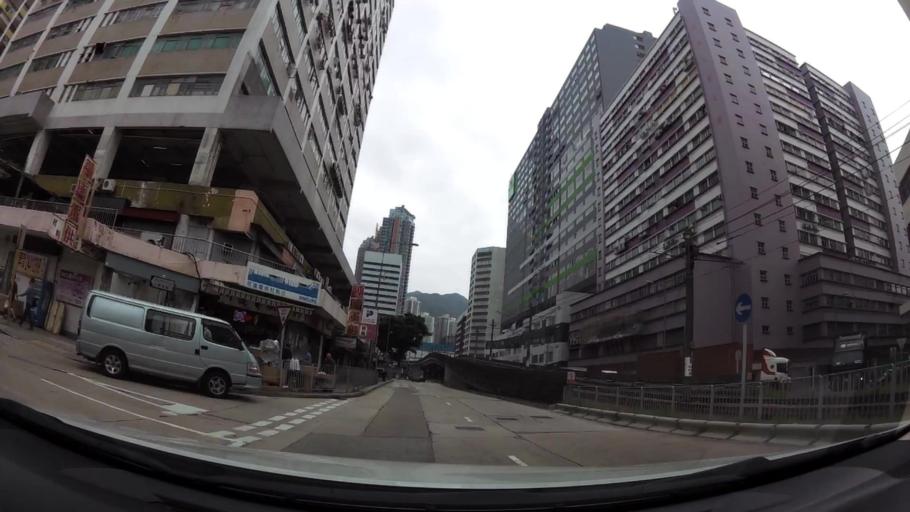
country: HK
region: Tuen Mun
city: Tuen Mun
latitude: 22.3951
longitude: 113.9696
